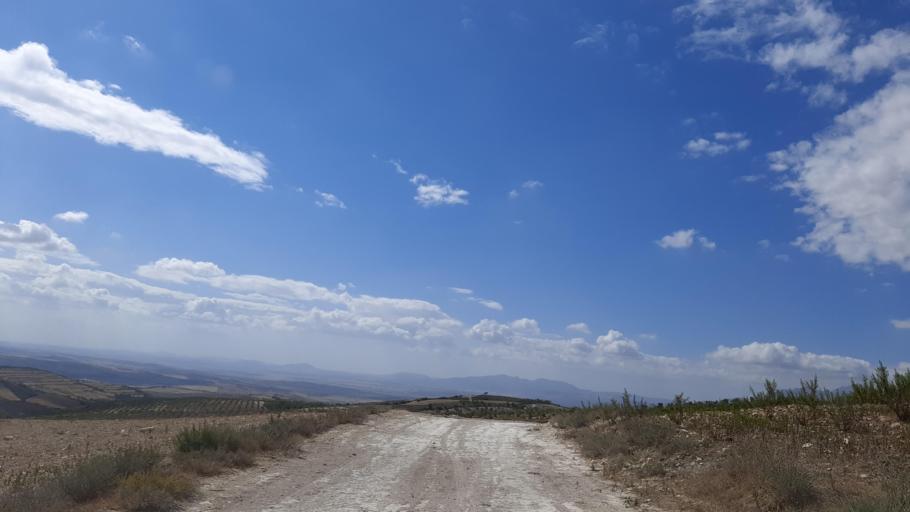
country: TN
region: Zaghwan
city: Zaghouan
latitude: 36.5064
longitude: 10.1845
